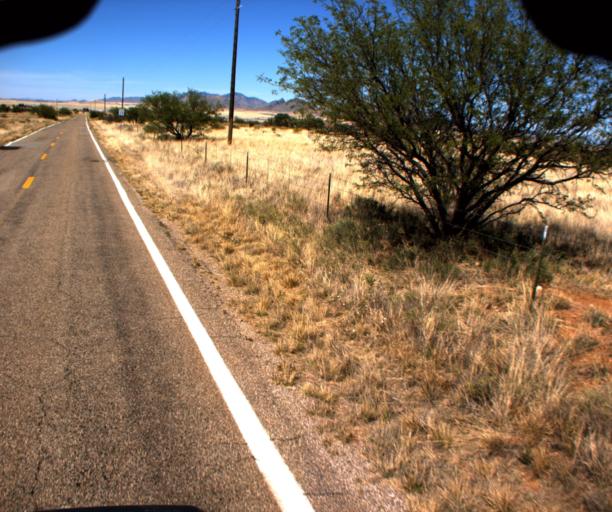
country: US
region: Arizona
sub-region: Cochise County
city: Huachuca City
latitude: 31.5919
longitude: -110.5601
